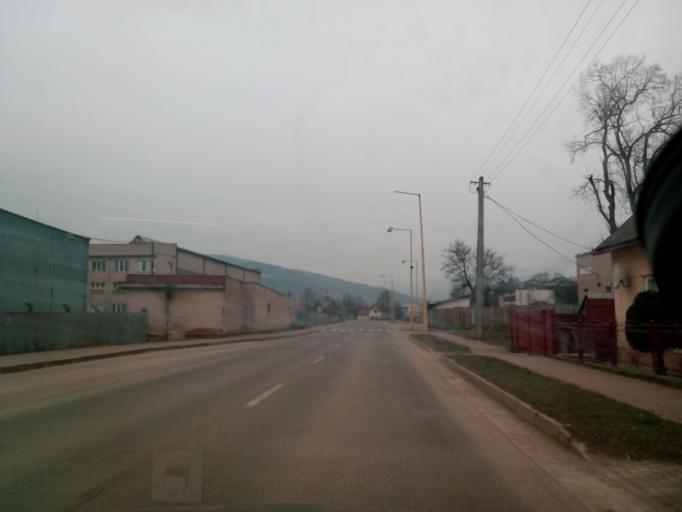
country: SK
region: Kosicky
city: Medzev
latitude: 48.6975
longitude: 20.9047
